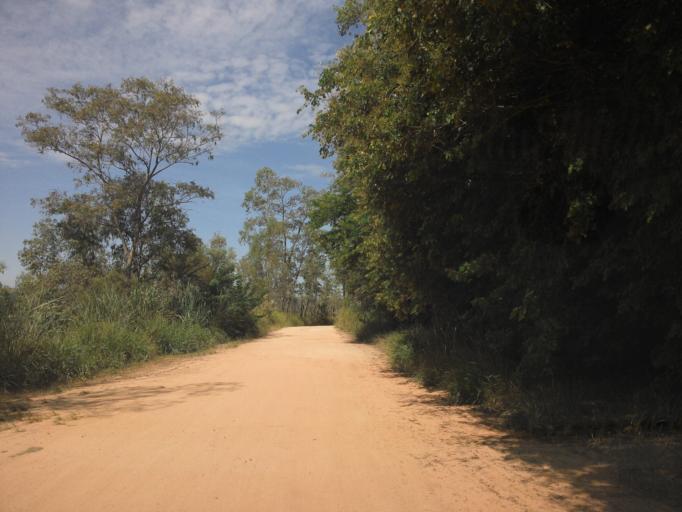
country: BR
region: Sao Paulo
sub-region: Valinhos
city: Valinhos
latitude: -22.9271
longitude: -46.9913
